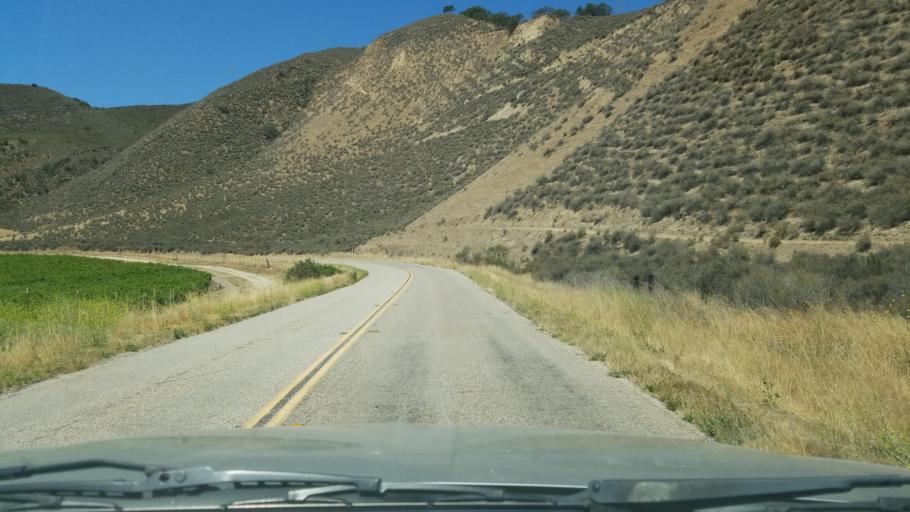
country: US
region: California
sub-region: Monterey County
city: Greenfield
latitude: 36.2785
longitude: -121.3306
